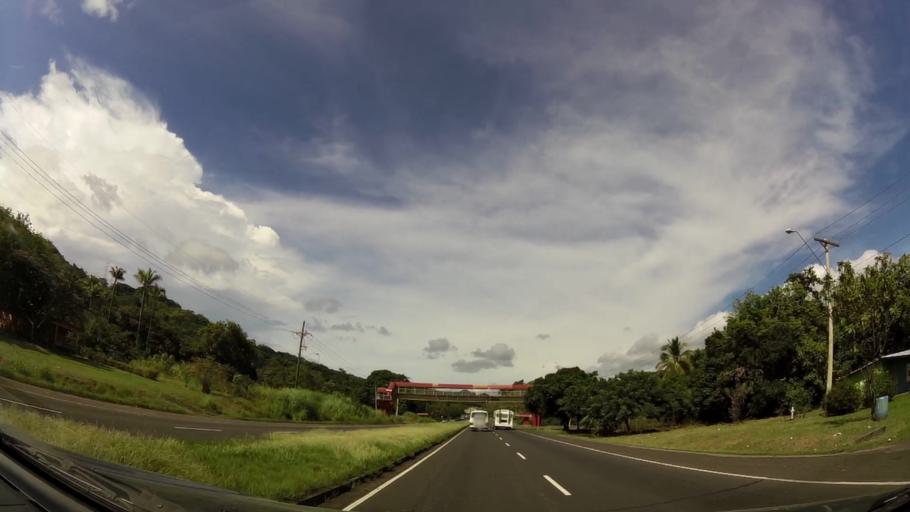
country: PA
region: Panama
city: Bejuco
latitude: 8.6662
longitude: -79.8718
